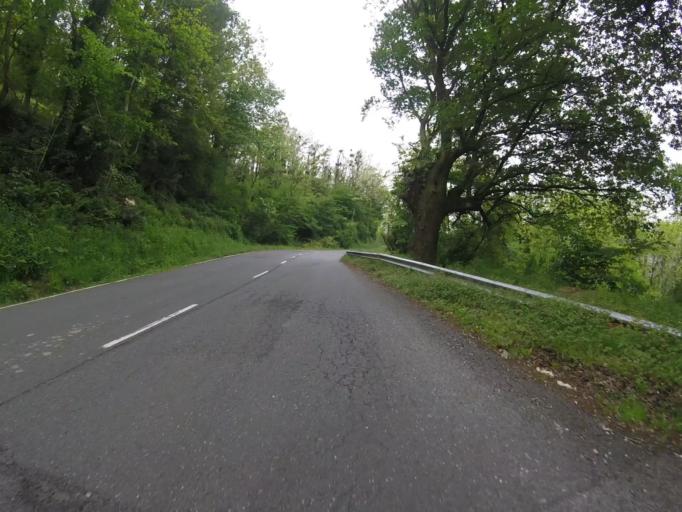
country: ES
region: Navarre
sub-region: Provincia de Navarra
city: Zugarramurdi
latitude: 43.2691
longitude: -1.4968
